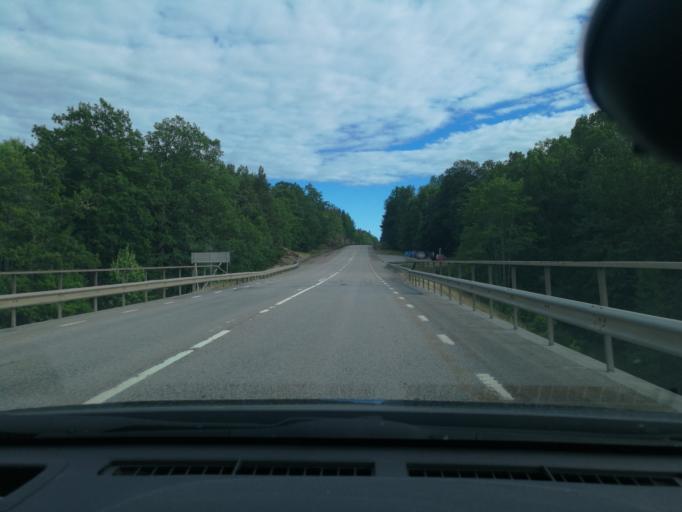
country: SE
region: Kalmar
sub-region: Vasterviks Kommun
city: Ankarsrum
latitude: 57.5501
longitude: 16.4766
